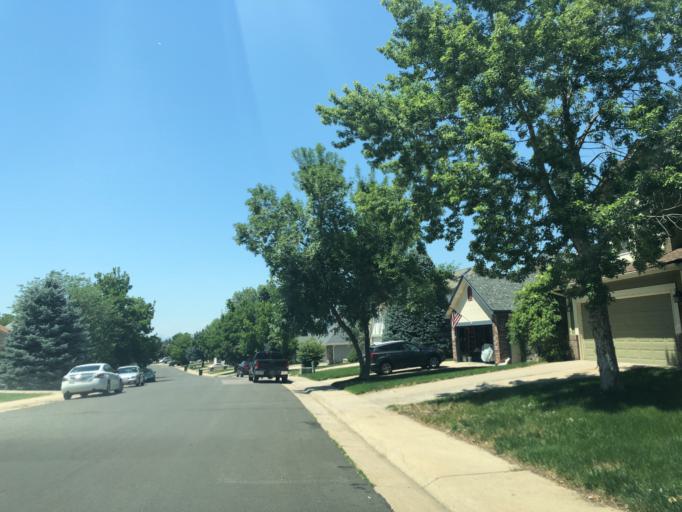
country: US
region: Colorado
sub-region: Arapahoe County
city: Dove Valley
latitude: 39.6297
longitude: -104.7728
